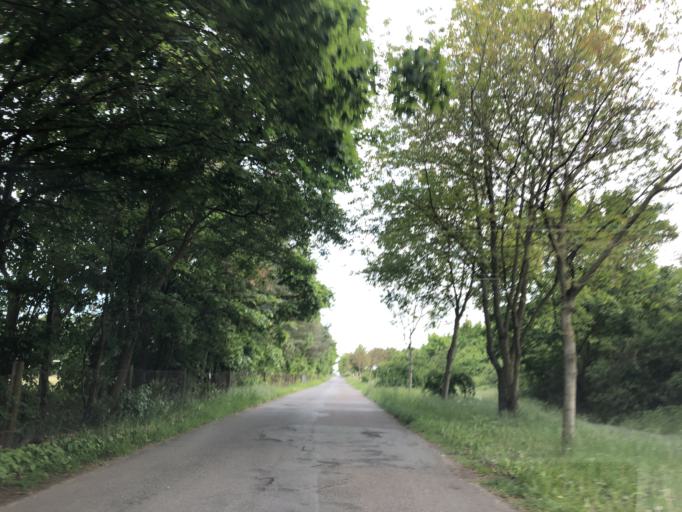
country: DE
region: Hesse
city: Weiterstadt
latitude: 49.9427
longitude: 8.6034
